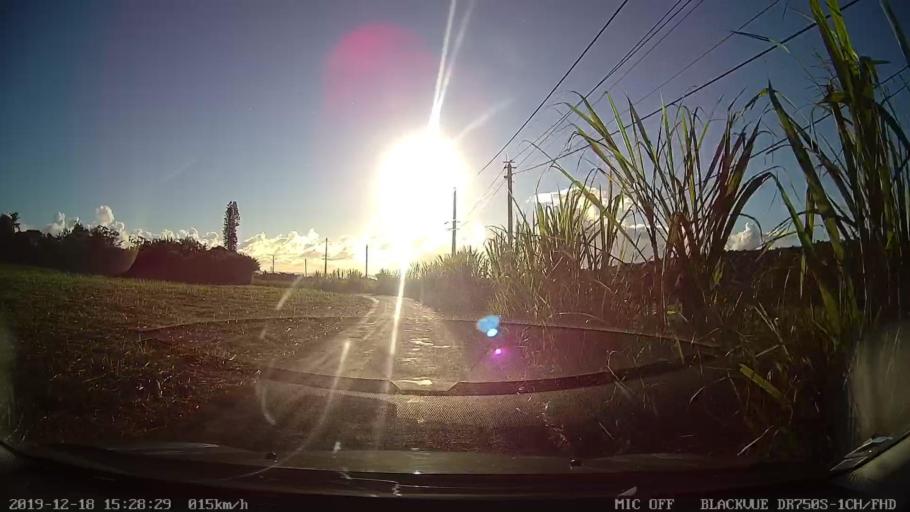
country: RE
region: Reunion
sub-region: Reunion
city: Bras-Panon
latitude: -20.9990
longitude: 55.6570
